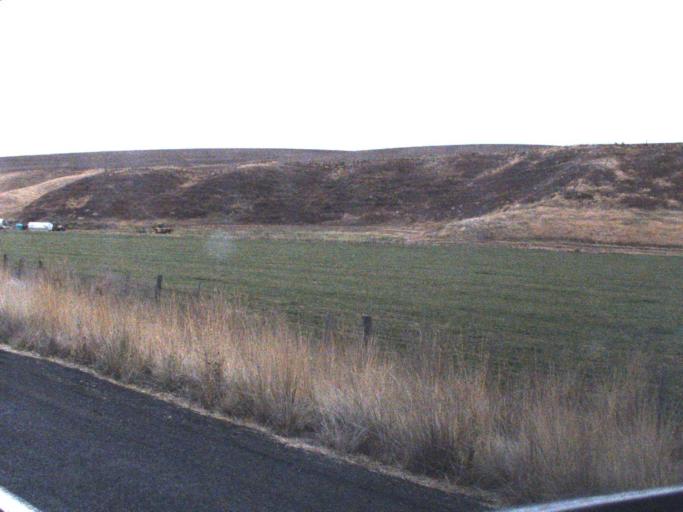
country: US
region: Washington
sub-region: Whitman County
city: Colfax
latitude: 46.8110
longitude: -117.5869
